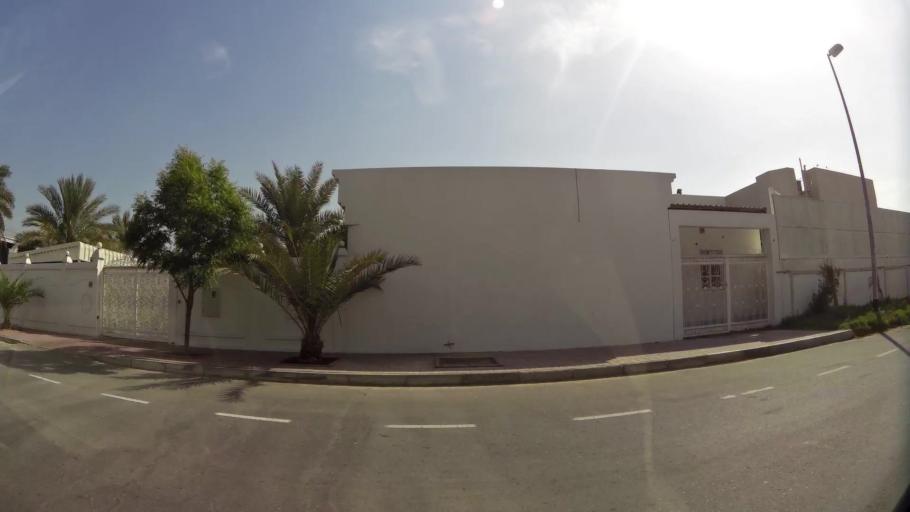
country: AE
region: Ash Shariqah
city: Sharjah
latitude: 25.2764
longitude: 55.4028
